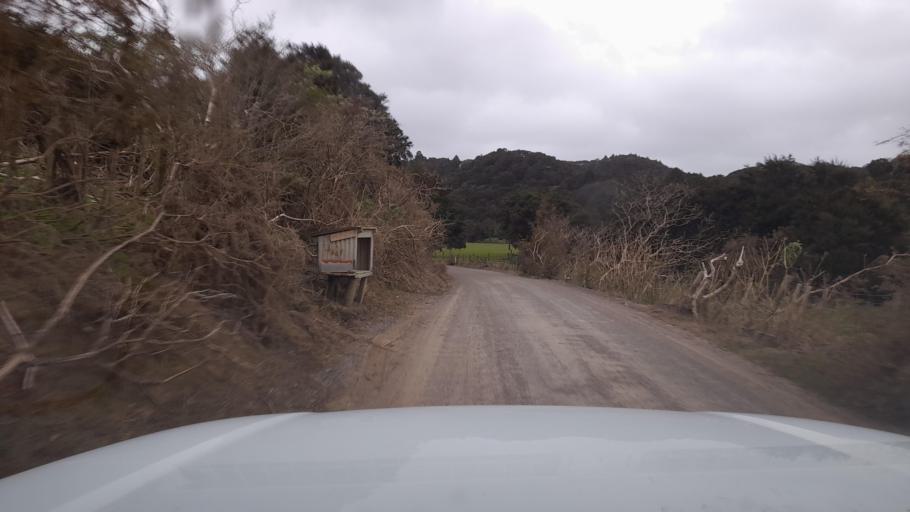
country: NZ
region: Northland
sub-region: Far North District
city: Paihia
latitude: -35.3515
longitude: 174.2262
